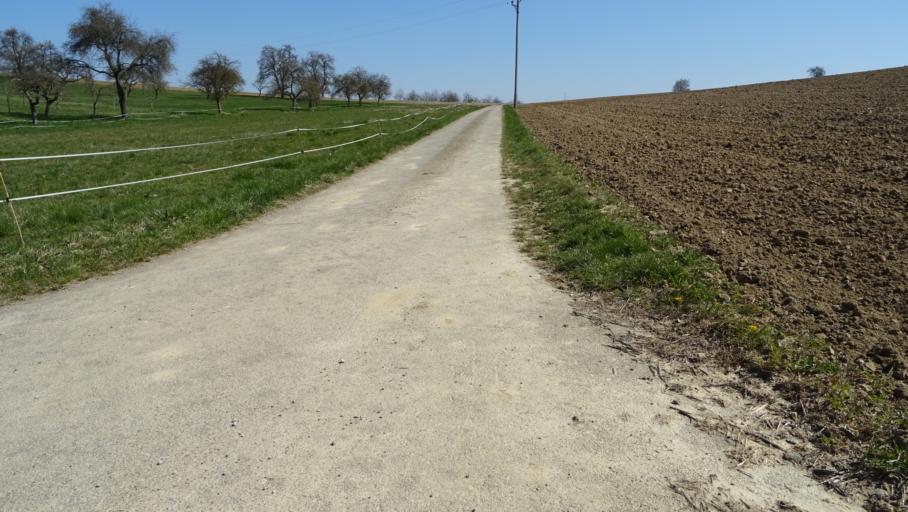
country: DE
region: Baden-Wuerttemberg
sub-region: Karlsruhe Region
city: Limbach
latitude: 49.4181
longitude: 9.2582
